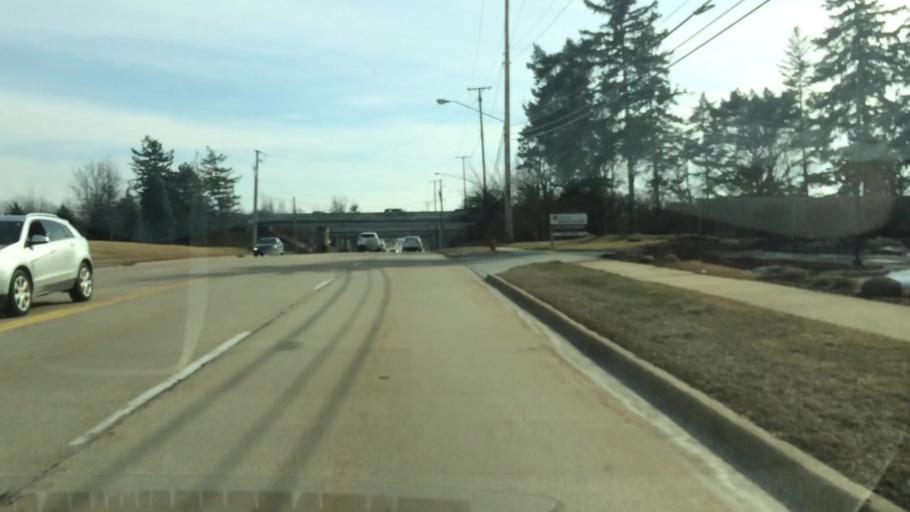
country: US
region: Ohio
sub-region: Cuyahoga County
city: Orange
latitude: 41.4311
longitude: -81.4980
